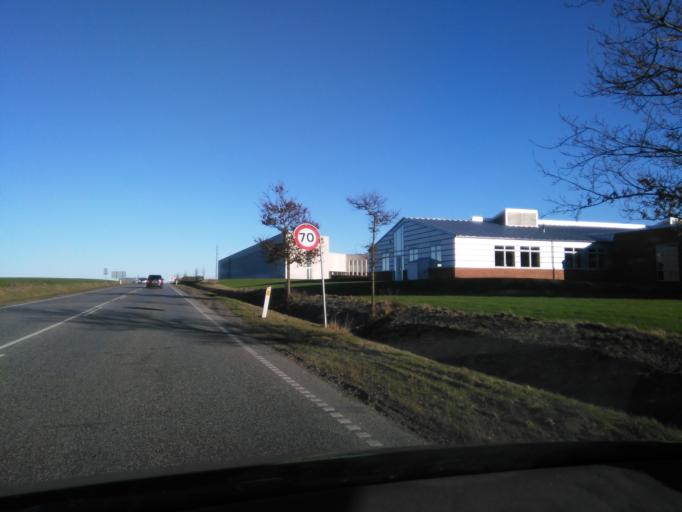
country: DK
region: North Denmark
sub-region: Mariagerfjord Kommune
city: Hobro
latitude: 56.6549
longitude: 9.7954
